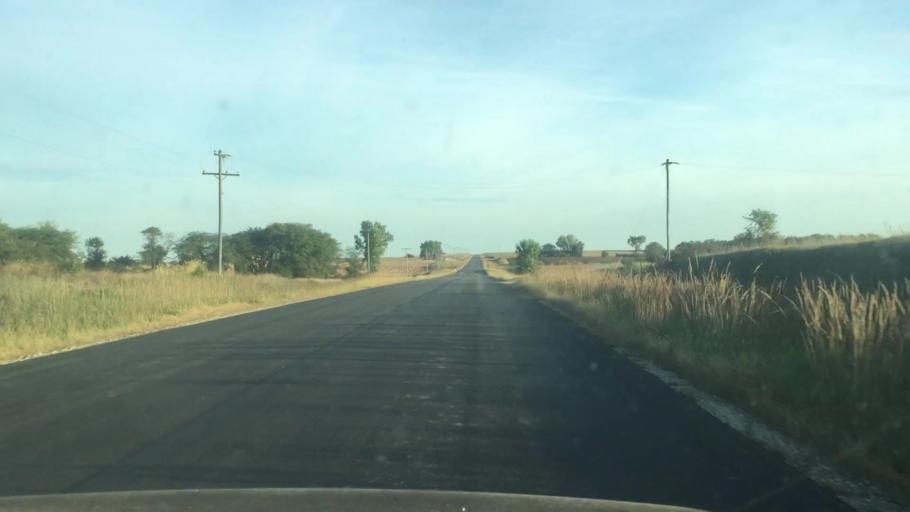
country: US
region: Kansas
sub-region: Marshall County
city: Marysville
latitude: 39.8796
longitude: -96.6009
